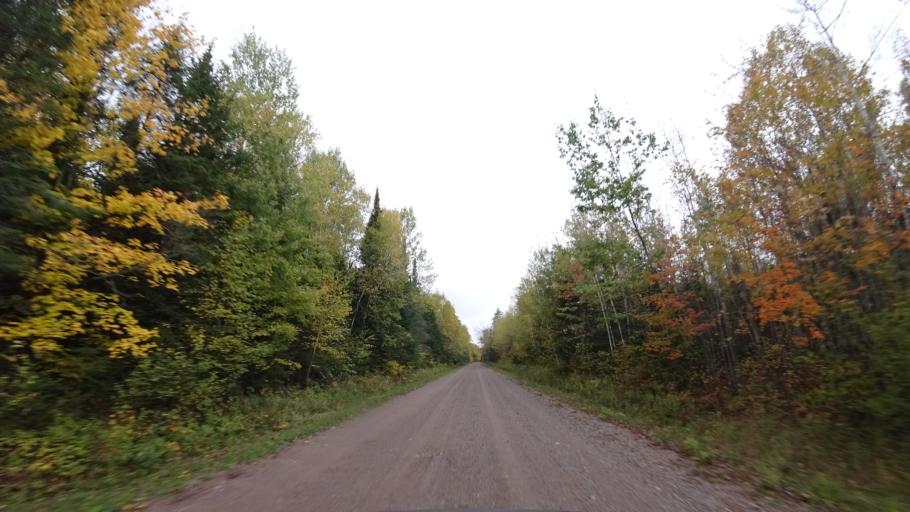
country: US
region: Wisconsin
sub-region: Sawyer County
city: Little Round Lake
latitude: 45.9726
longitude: -90.9846
